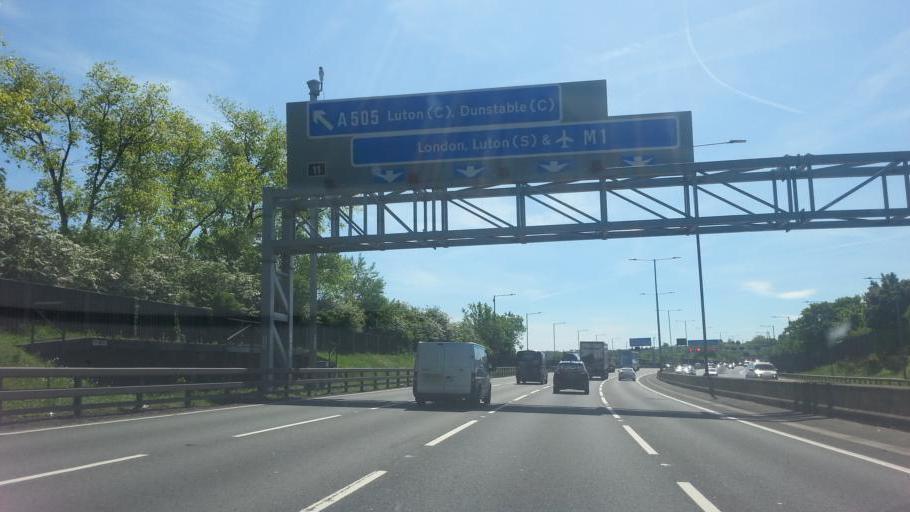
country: GB
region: England
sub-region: Central Bedfordshire
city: Caddington
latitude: 51.8985
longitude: -0.4713
